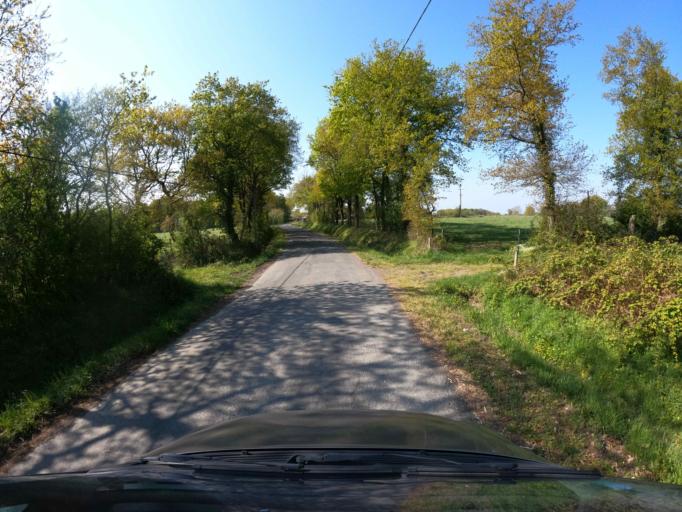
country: FR
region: Pays de la Loire
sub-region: Departement de la Loire-Atlantique
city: Aigrefeuille-sur-Maine
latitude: 47.0813
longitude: -1.4189
